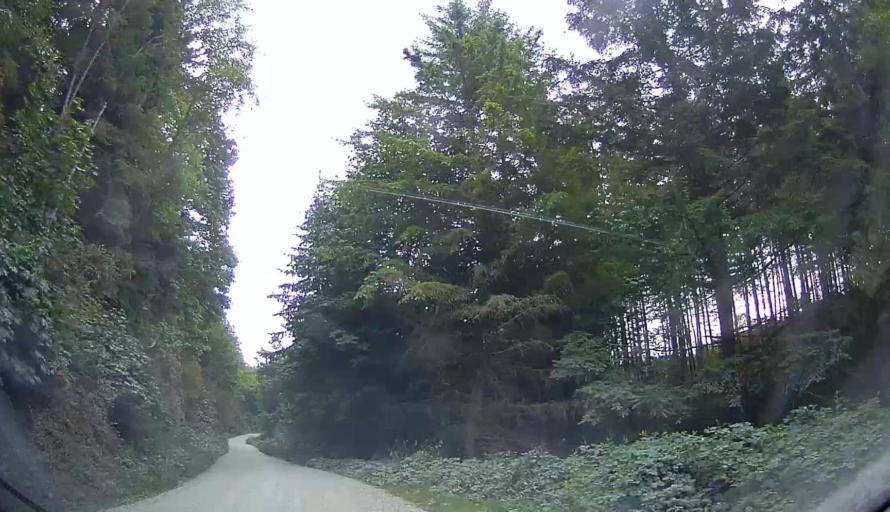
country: US
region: Washington
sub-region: Whatcom County
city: Sudden Valley
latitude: 48.6135
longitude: -122.3869
